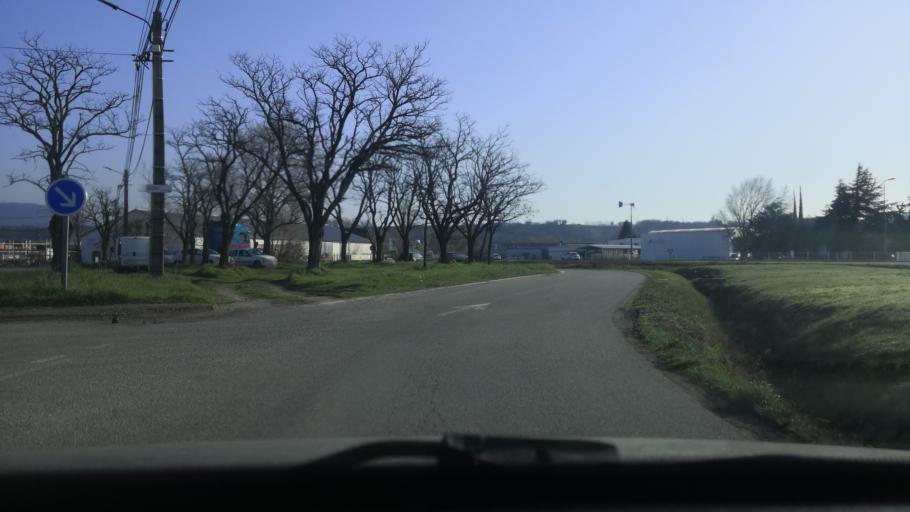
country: FR
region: Rhone-Alpes
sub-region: Departement de la Drome
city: Ancone
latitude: 44.5798
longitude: 4.7450
